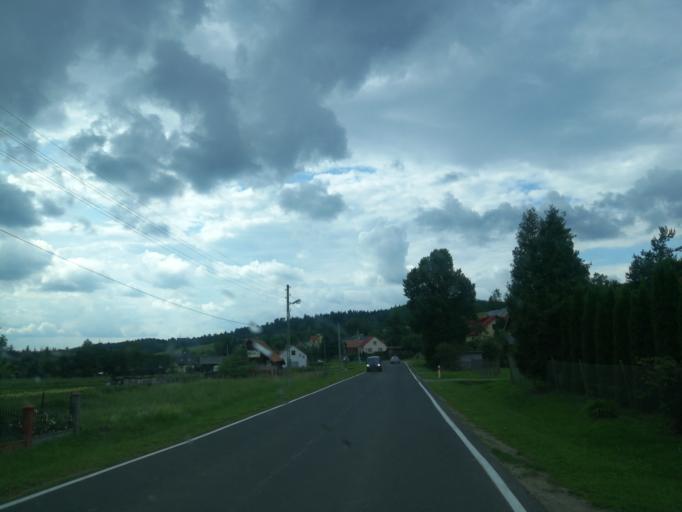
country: PL
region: Subcarpathian Voivodeship
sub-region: Powiat leski
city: Olszanica
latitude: 49.4467
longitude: 22.4441
